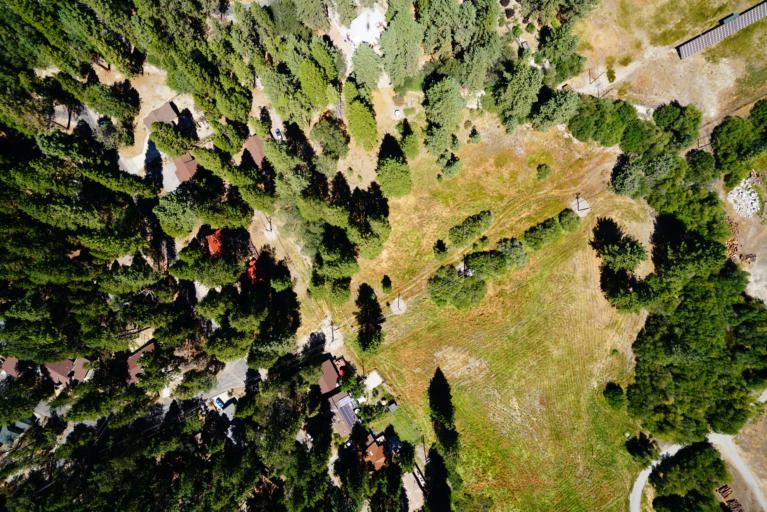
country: US
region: California
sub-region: Riverside County
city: Idyllwild-Pine Cove
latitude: 33.7555
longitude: -116.7314
